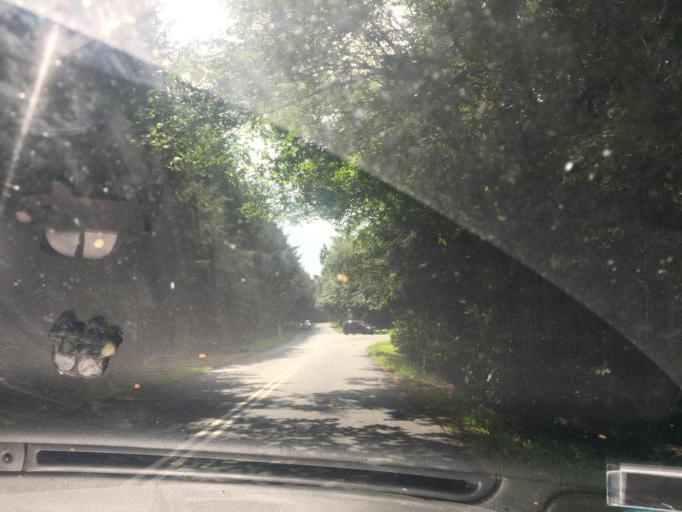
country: DK
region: Capital Region
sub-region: Allerod Kommune
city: Blovstrod
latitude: 55.8461
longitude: 12.3887
